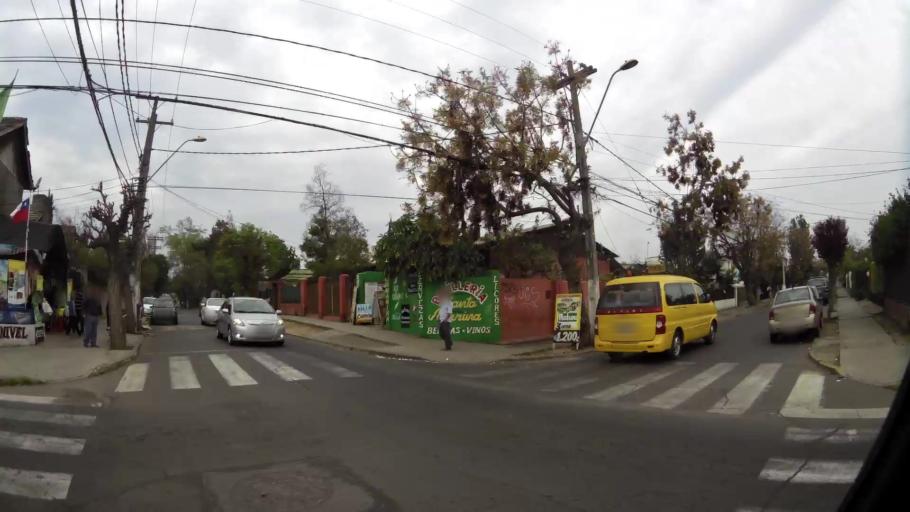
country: CL
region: Santiago Metropolitan
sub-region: Provincia de Santiago
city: Lo Prado
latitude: -33.5037
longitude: -70.7619
